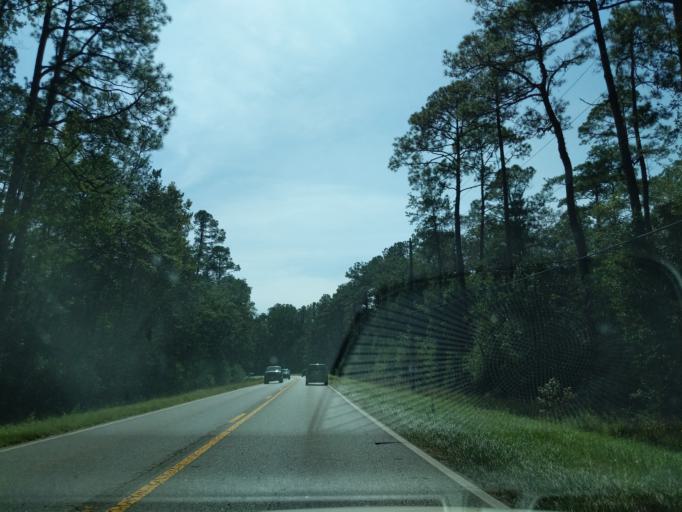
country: US
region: Florida
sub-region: Okaloosa County
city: Crestview
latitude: 30.7423
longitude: -86.6222
